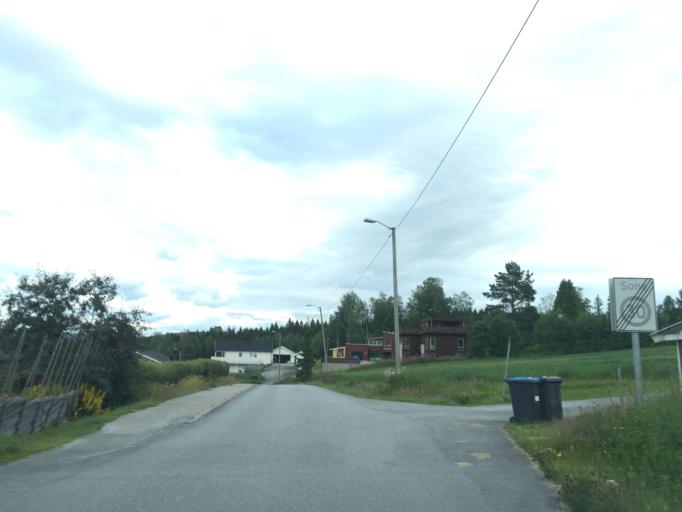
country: NO
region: Hedmark
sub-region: Kongsvinger
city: Kongsvinger
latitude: 60.1803
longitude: 11.9907
